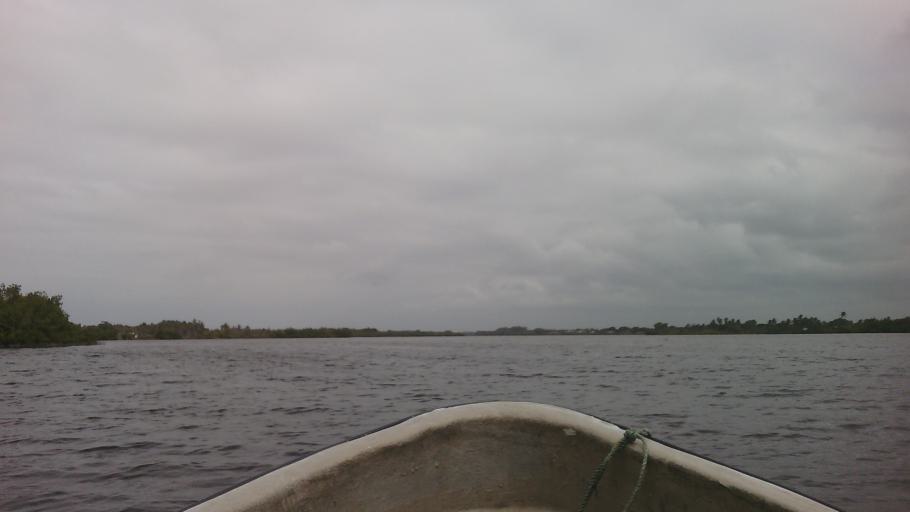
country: BJ
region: Atlantique
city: Hevie
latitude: 6.3504
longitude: 2.2862
